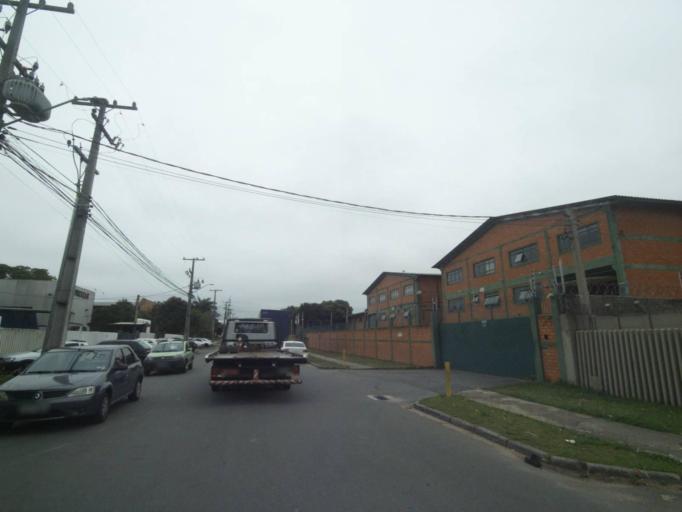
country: BR
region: Parana
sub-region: Araucaria
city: Araucaria
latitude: -25.5480
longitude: -49.3311
